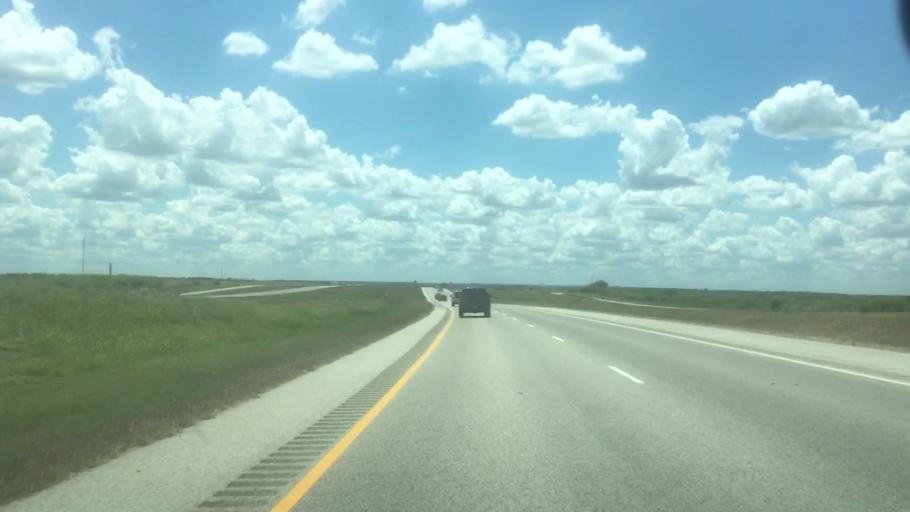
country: US
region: Texas
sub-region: Caldwell County
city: Martindale
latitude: 29.8022
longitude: -97.7775
